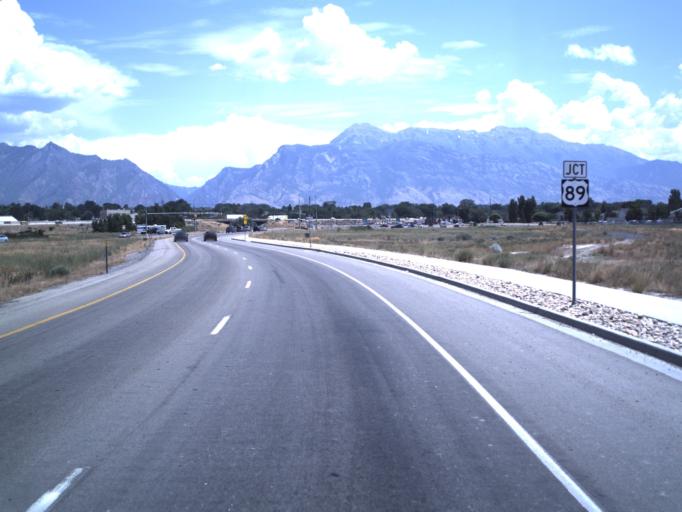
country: US
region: Utah
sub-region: Utah County
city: Lehi
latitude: 40.4125
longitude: -111.8762
